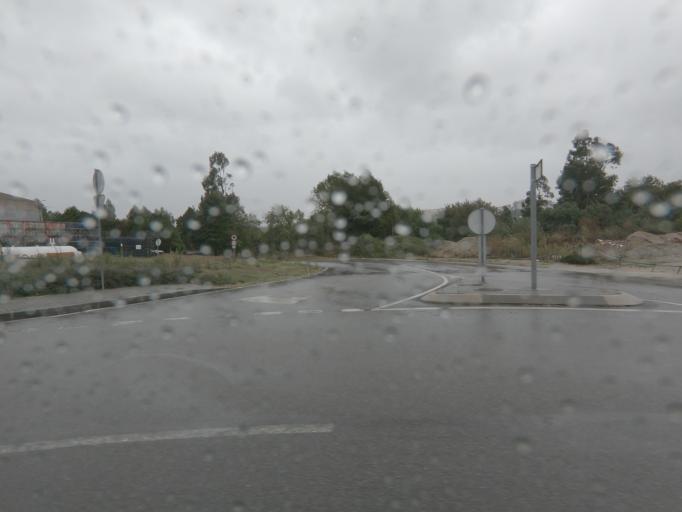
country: PT
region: Porto
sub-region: Penafiel
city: Penafiel
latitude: 41.1953
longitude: -8.3060
